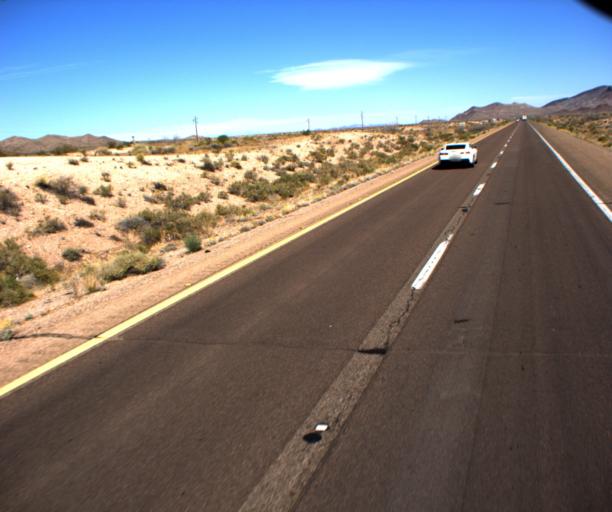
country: US
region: Nevada
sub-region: Clark County
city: Boulder City
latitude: 35.8132
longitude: -114.5462
